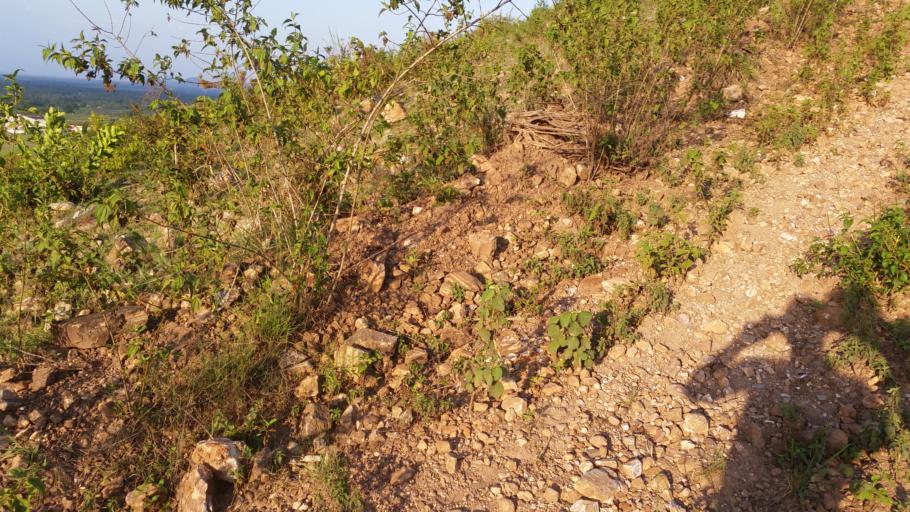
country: UG
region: Eastern Region
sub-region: Busia District
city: Busia
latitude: 0.5420
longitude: 34.0158
